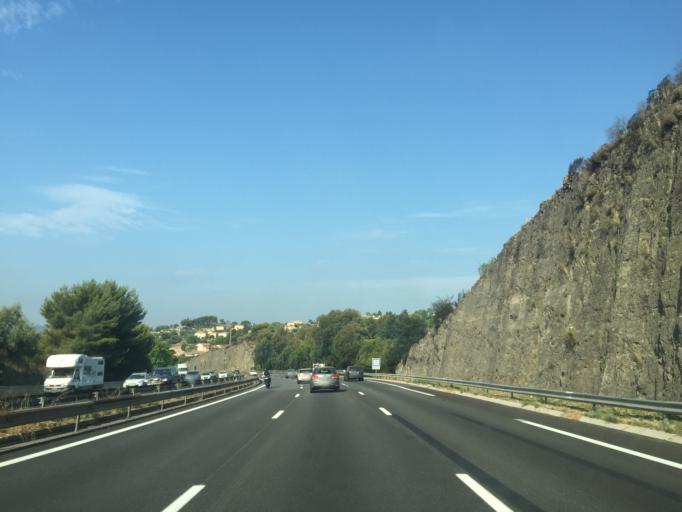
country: FR
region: Provence-Alpes-Cote d'Azur
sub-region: Departement des Alpes-Maritimes
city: Biot
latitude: 43.6320
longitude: 7.1205
